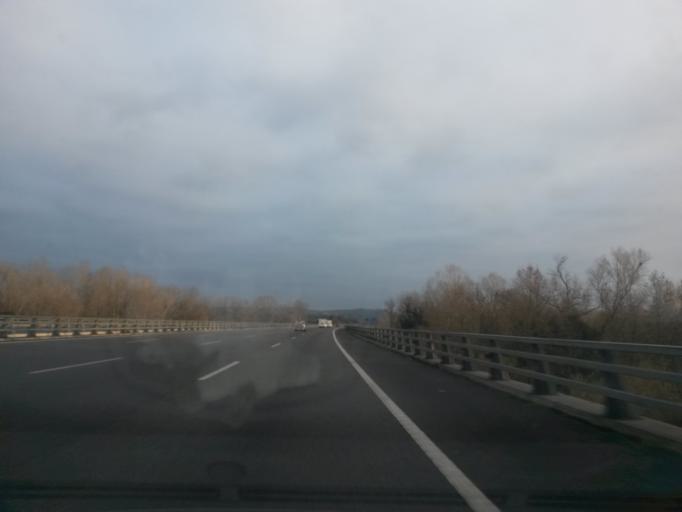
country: ES
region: Catalonia
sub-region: Provincia de Girona
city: Salt
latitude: 41.9820
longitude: 2.7814
